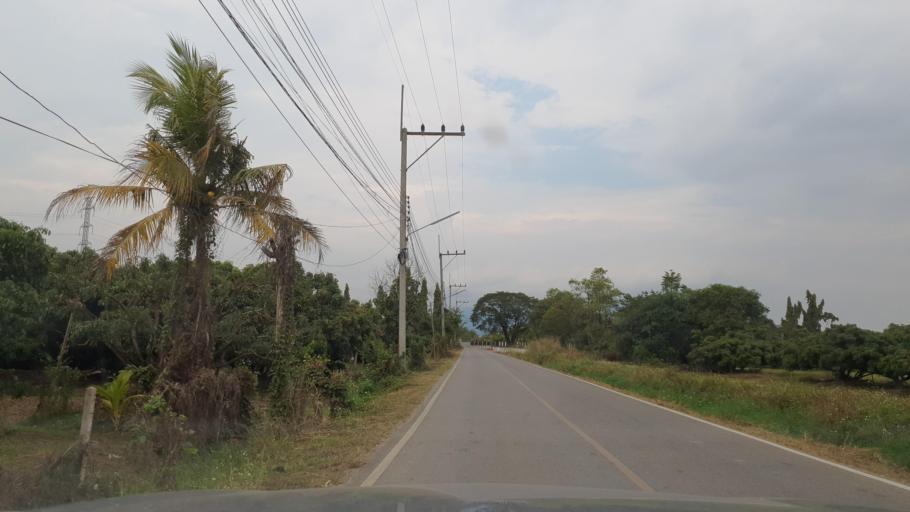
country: TH
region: Chiang Mai
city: Hang Dong
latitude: 18.6804
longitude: 98.9418
